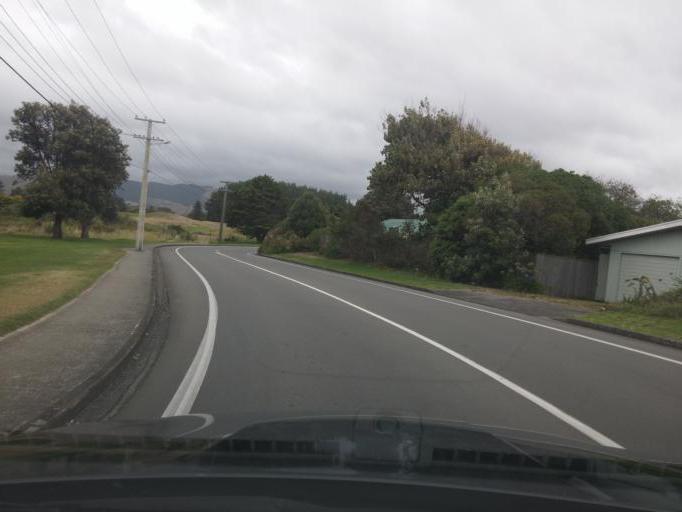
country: NZ
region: Wellington
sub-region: Kapiti Coast District
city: Paraparaumu
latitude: -40.8604
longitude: 175.0288
